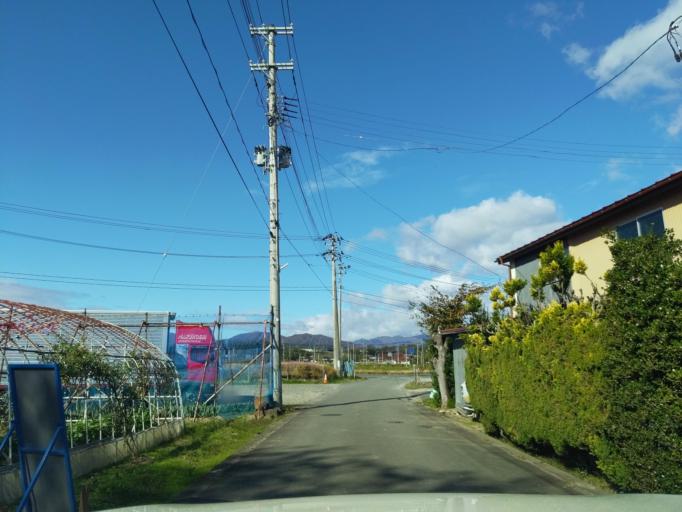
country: JP
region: Fukushima
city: Koriyama
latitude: 37.4539
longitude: 140.3157
